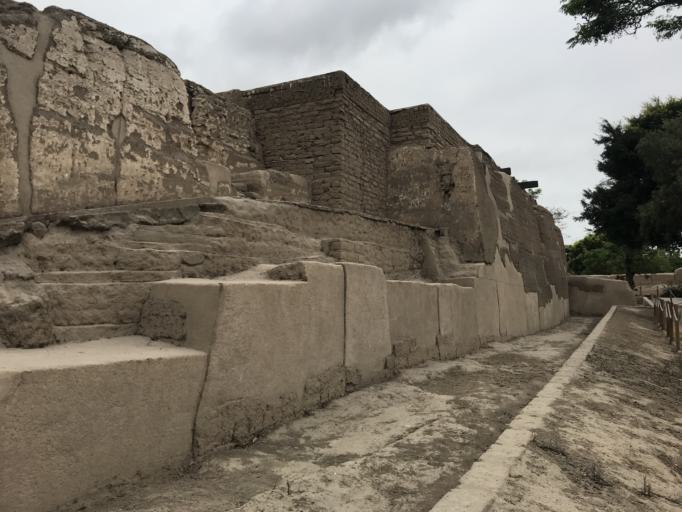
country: PE
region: Callao
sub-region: Callao
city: Callao
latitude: -12.0693
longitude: -77.0899
